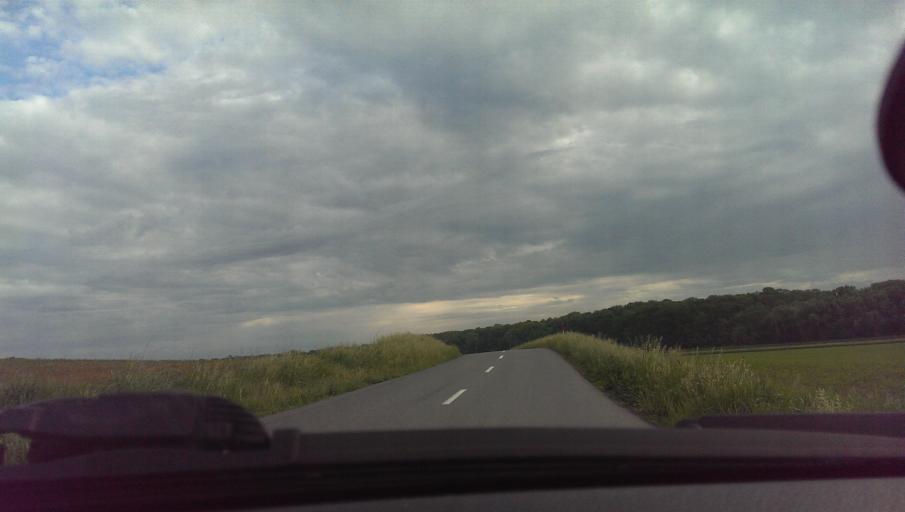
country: CZ
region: Zlin
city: Zlutava
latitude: 49.2217
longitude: 17.4886
